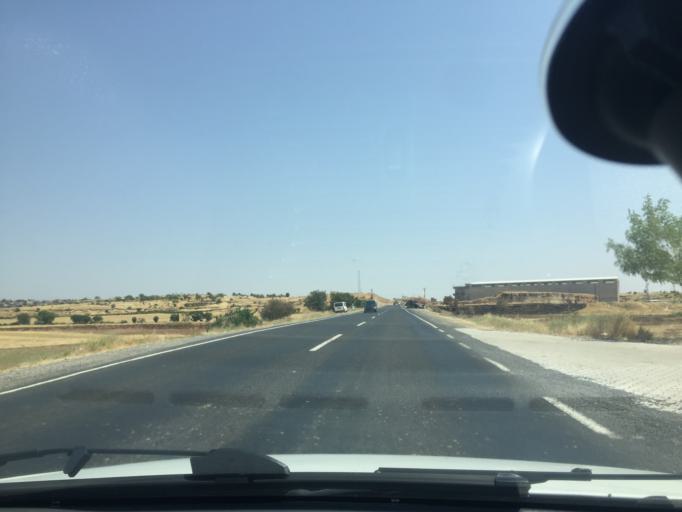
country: TR
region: Mardin
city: Acirli
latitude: 37.4481
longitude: 41.2743
